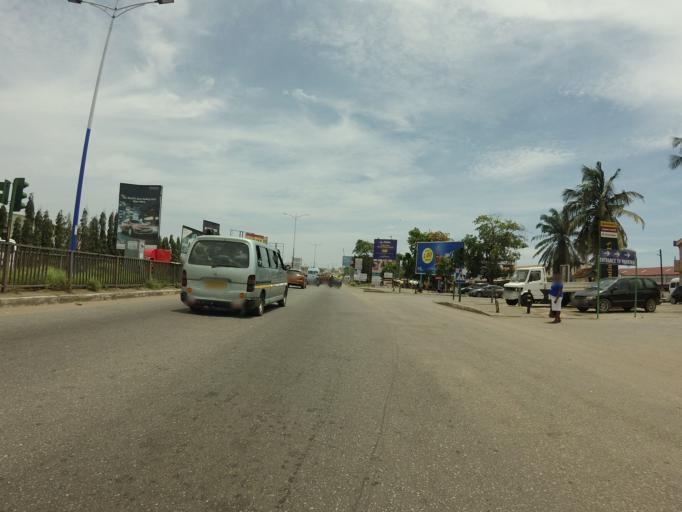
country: GH
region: Greater Accra
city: Accra
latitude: 5.5573
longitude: -0.2228
